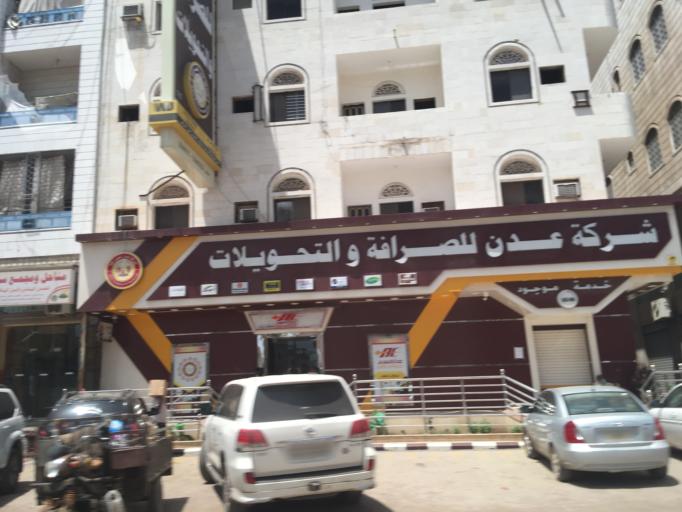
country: YE
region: Aden
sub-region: Al Mansura
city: Al Mansurah
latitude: 12.8627
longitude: 44.9716
